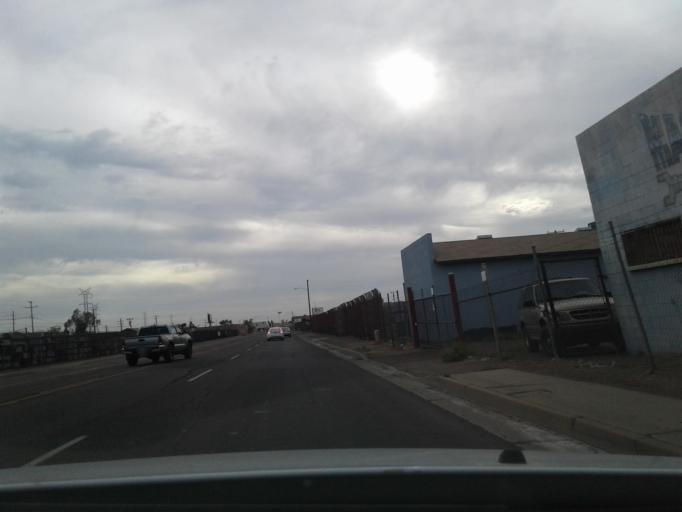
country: US
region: Arizona
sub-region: Maricopa County
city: Phoenix
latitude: 33.4414
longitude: -112.1028
